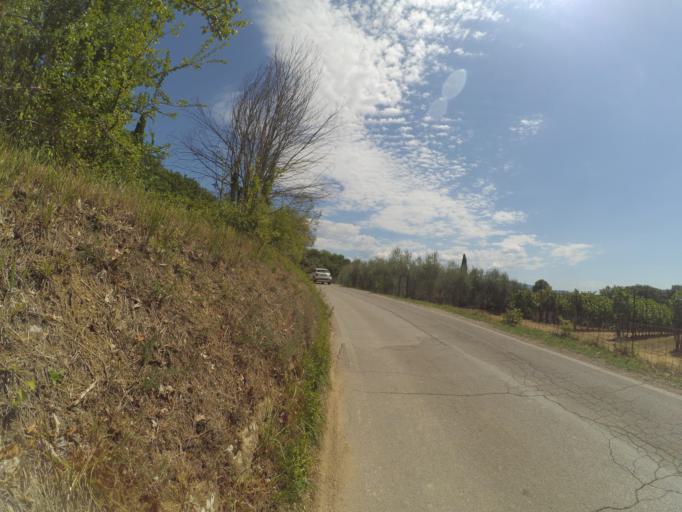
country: IT
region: Tuscany
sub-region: Province of Arezzo
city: Castiglion Fibocchi
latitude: 43.5306
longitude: 11.7696
